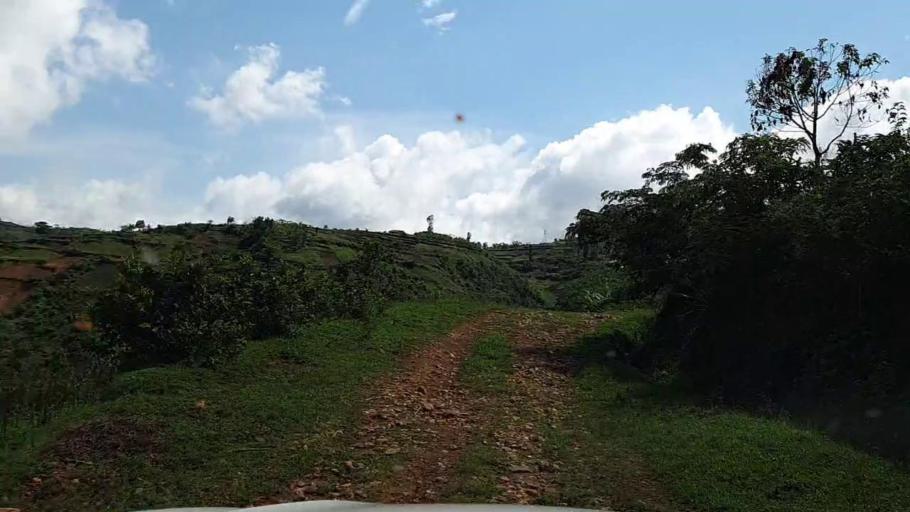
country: RW
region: Southern Province
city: Gikongoro
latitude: -2.3605
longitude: 29.5391
